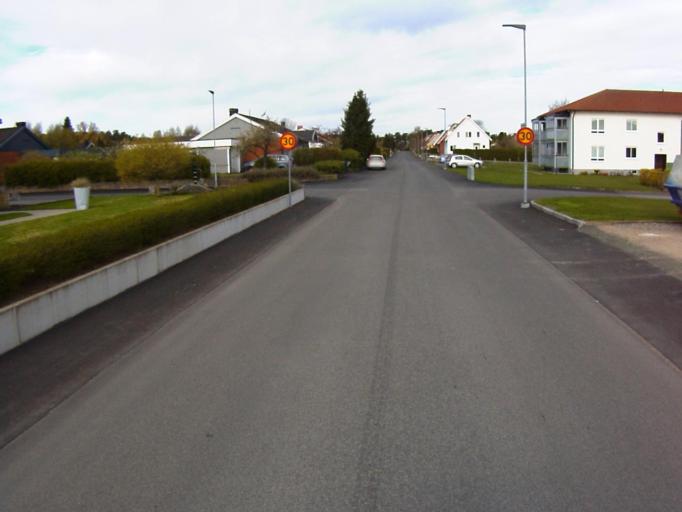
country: SE
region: Skane
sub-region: Kristianstads Kommun
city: Norra Asum
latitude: 55.9922
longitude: 14.1459
